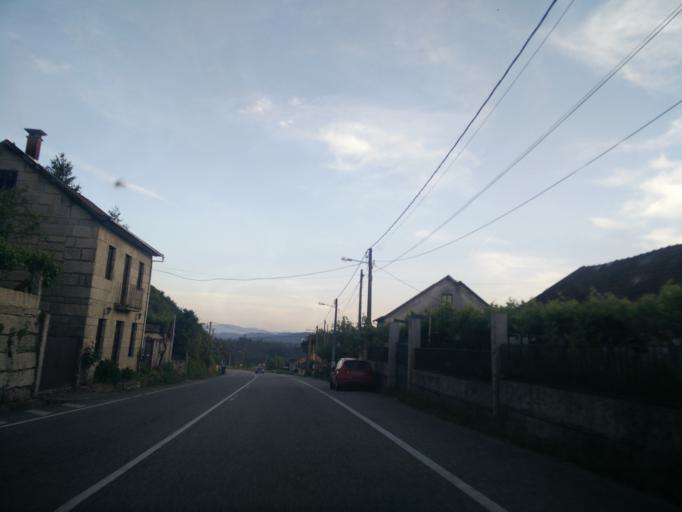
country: ES
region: Galicia
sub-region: Provincia de Pontevedra
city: Ponteareas
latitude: 42.2069
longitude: -8.5095
